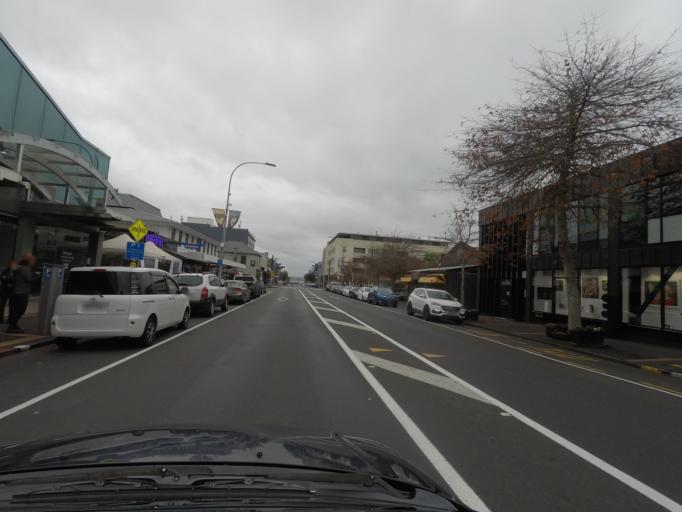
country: NZ
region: Auckland
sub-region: Auckland
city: Auckland
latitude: -36.8550
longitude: 174.7802
